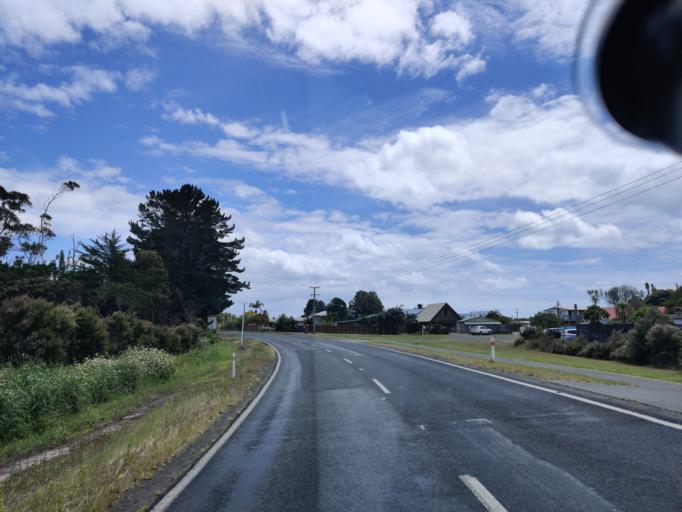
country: NZ
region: Northland
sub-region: Far North District
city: Kaitaia
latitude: -34.8242
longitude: 173.1276
